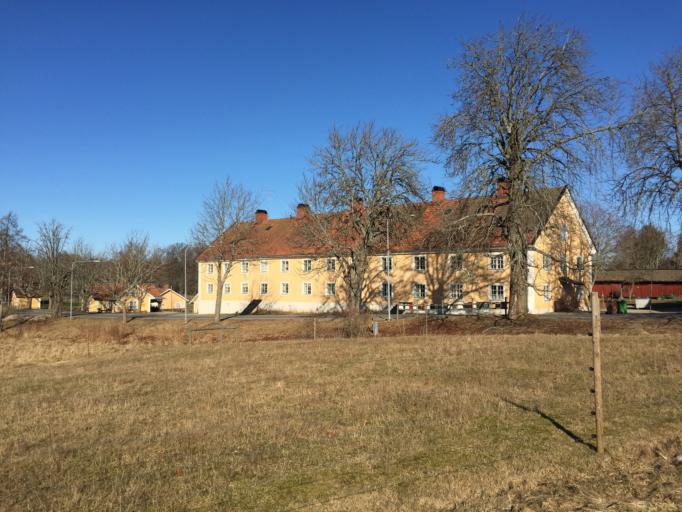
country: SE
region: OErebro
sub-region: Orebro Kommun
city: Odensbacken
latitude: 59.0104
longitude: 15.5824
